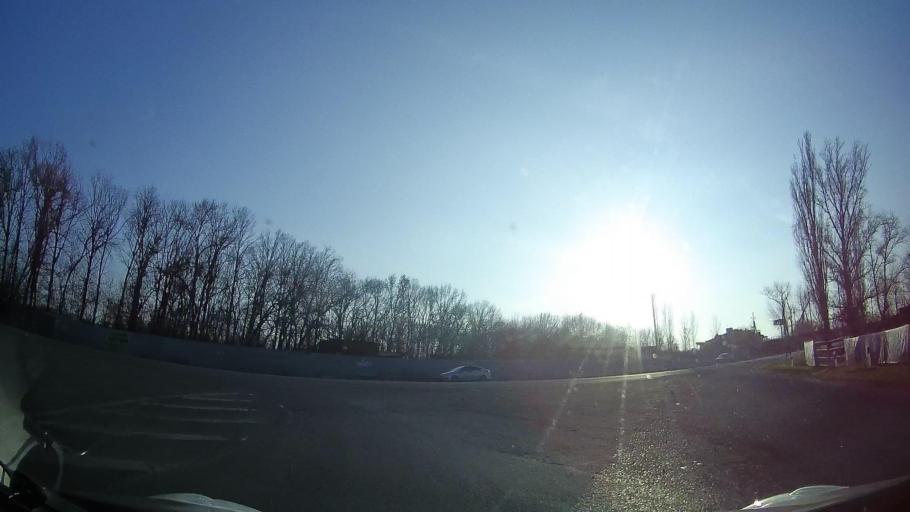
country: RU
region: Rostov
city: Ol'ginskaya
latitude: 47.1294
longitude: 39.8805
